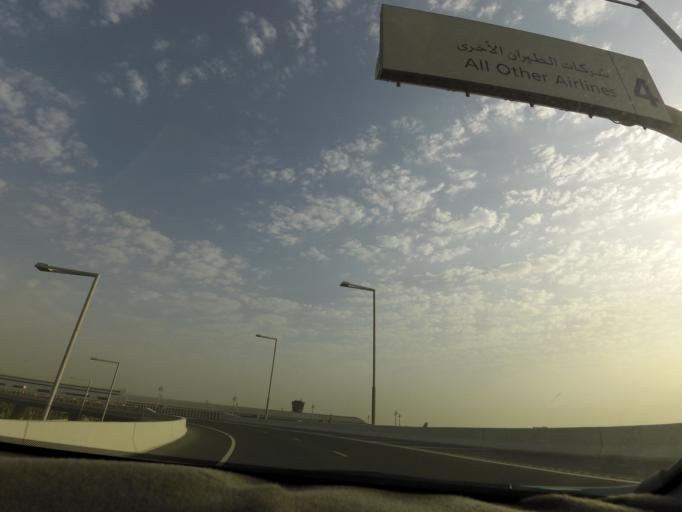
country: QA
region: Al Wakrah
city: Al Wakrah
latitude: 25.2595
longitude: 51.6173
